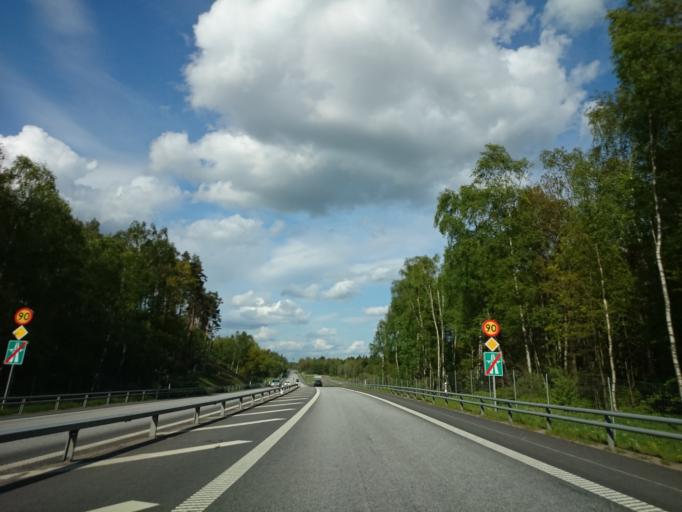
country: SE
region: Skane
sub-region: Horby Kommun
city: Hoerby
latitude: 55.9209
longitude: 13.7868
